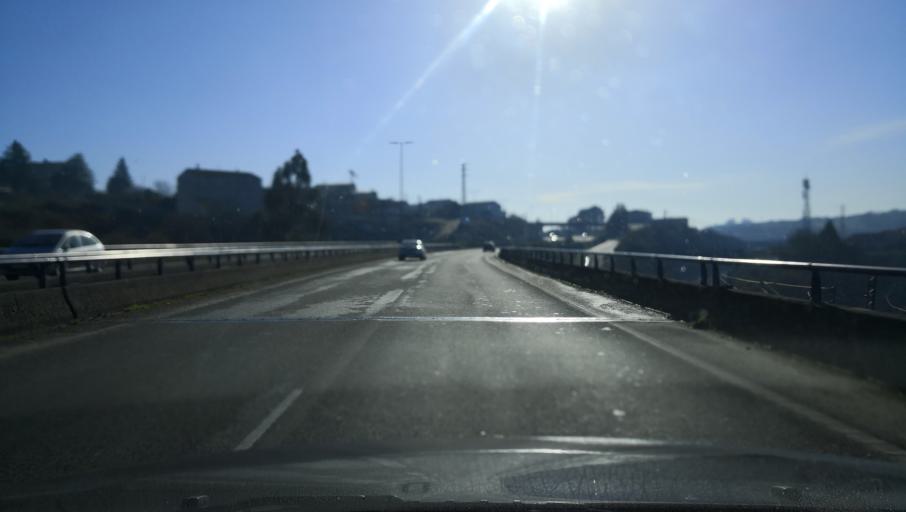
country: ES
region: Galicia
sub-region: Provincia da Coruna
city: Santiago de Compostela
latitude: 42.8625
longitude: -8.5494
